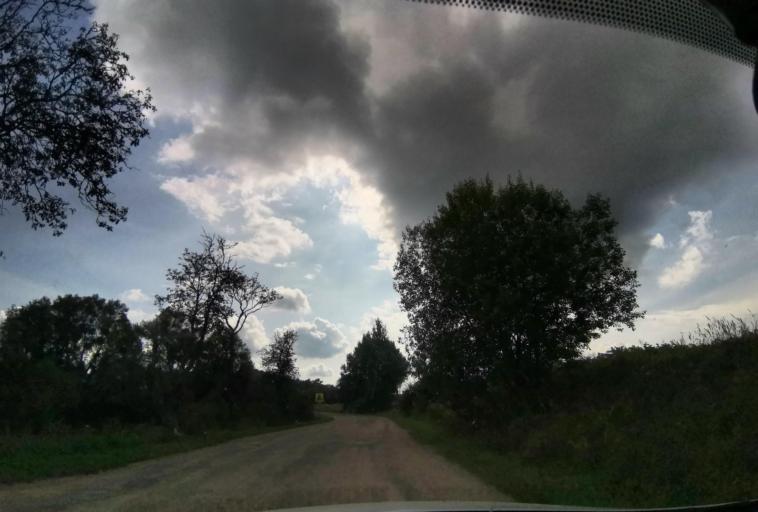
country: PL
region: Warmian-Masurian Voivodeship
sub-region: Powiat goldapski
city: Goldap
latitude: 54.4204
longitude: 22.3986
